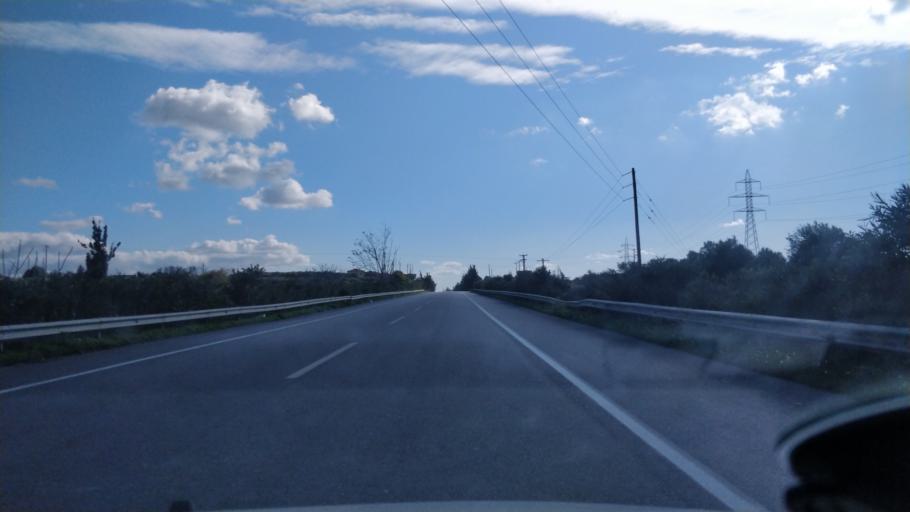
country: GR
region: Crete
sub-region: Nomos Irakleiou
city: Skalanion
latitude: 35.2982
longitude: 25.1762
